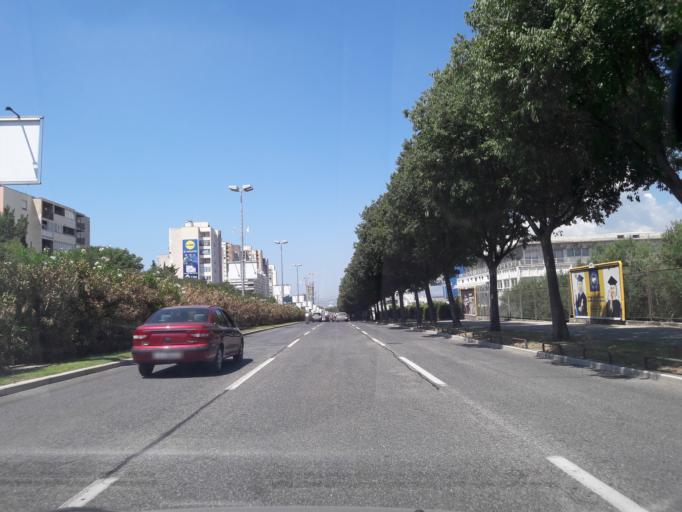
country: HR
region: Splitsko-Dalmatinska
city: Vranjic
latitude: 43.5195
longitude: 16.4706
